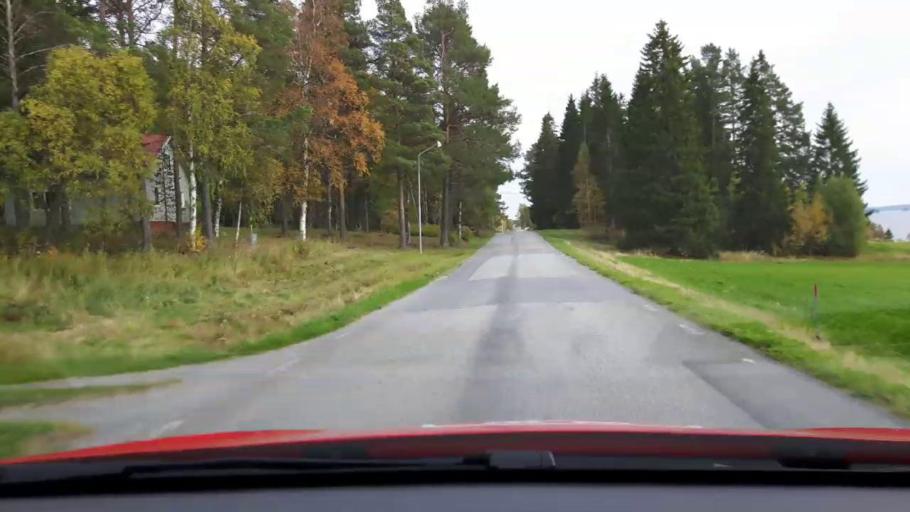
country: SE
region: Jaemtland
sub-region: Krokoms Kommun
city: Valla
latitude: 63.2561
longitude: 14.0216
